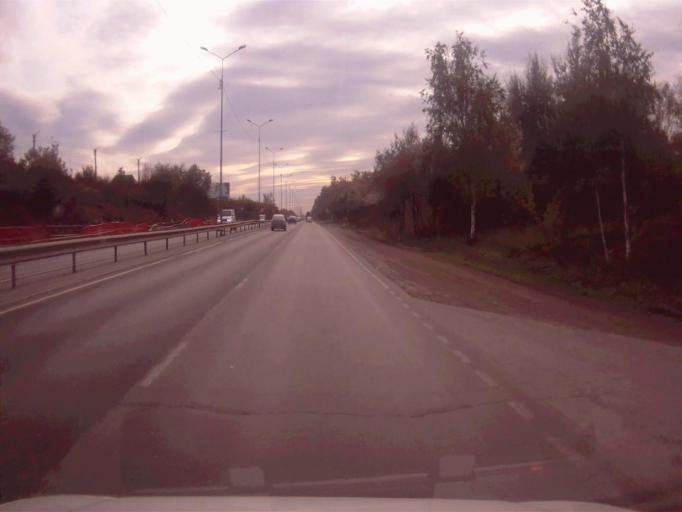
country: RU
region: Chelyabinsk
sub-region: Gorod Chelyabinsk
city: Chelyabinsk
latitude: 55.1063
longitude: 61.4073
